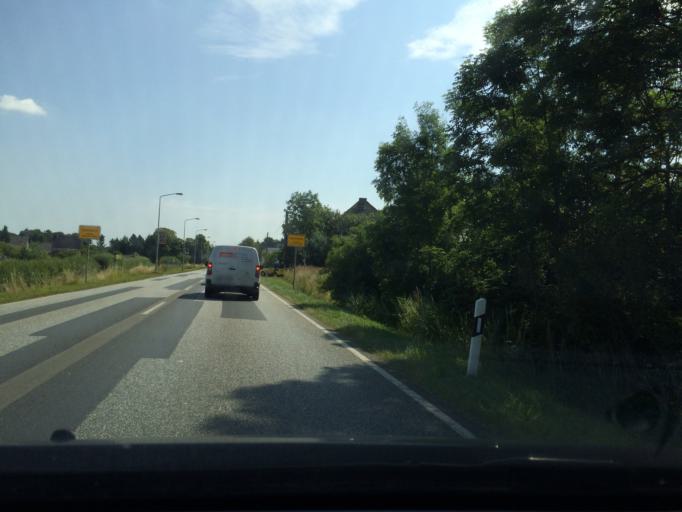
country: DE
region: Mecklenburg-Vorpommern
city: Samtens
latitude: 54.3546
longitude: 13.2849
